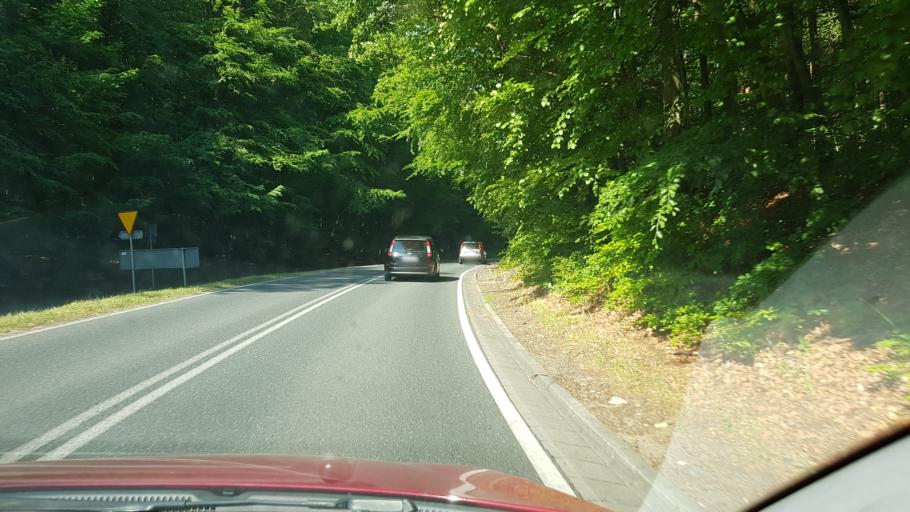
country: PL
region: West Pomeranian Voivodeship
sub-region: Powiat kamienski
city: Miedzyzdroje
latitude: 53.9379
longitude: 14.4751
